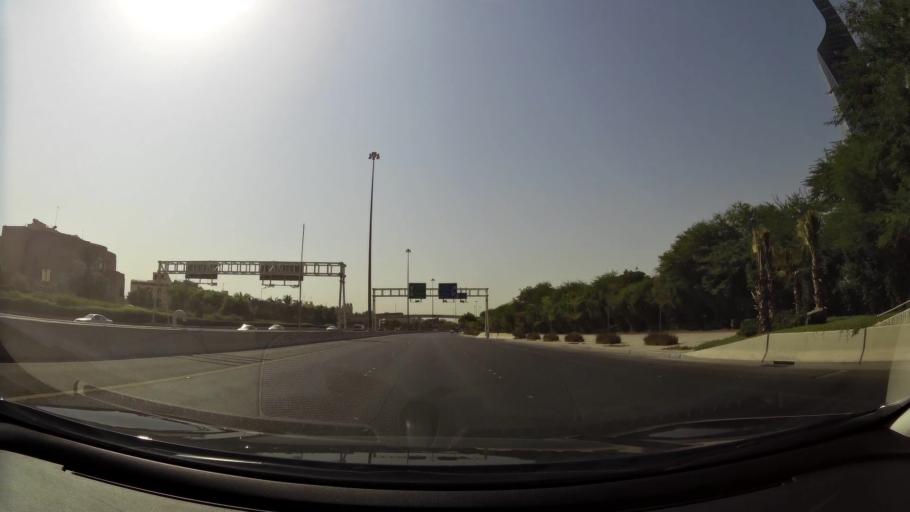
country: KW
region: Al Asimah
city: Ad Dasmah
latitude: 29.3708
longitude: 47.9956
